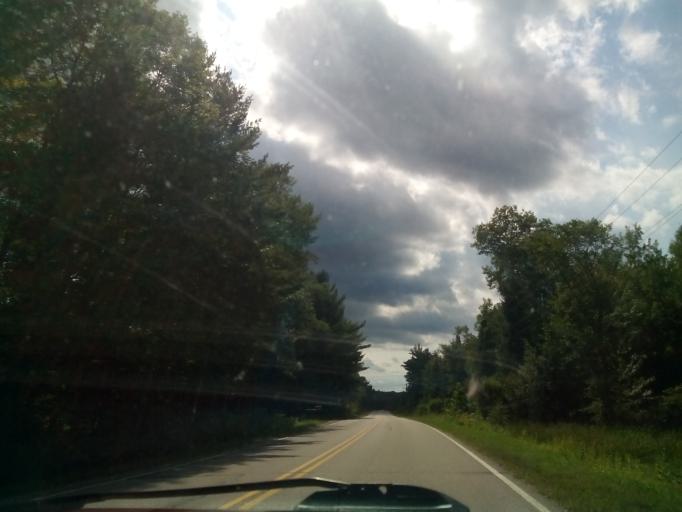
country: US
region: Wisconsin
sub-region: Marinette County
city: Niagara
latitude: 45.4976
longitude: -87.9741
